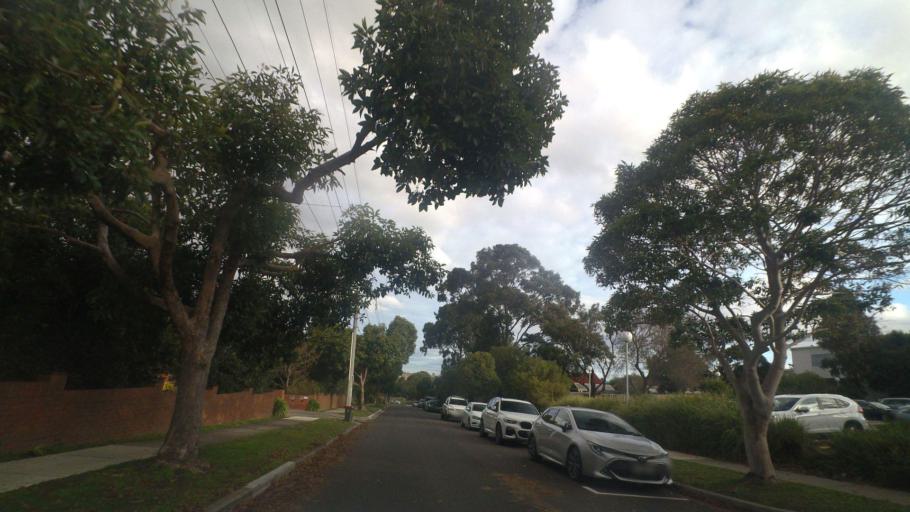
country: AU
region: Victoria
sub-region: Manningham
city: Doncaster East
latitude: -37.7872
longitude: 145.1416
